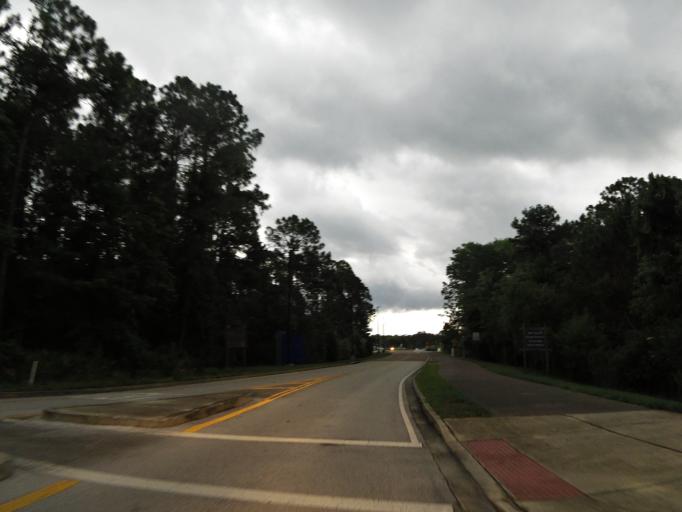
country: US
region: Florida
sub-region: Duval County
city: Jacksonville Beach
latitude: 30.2762
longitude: -81.5144
